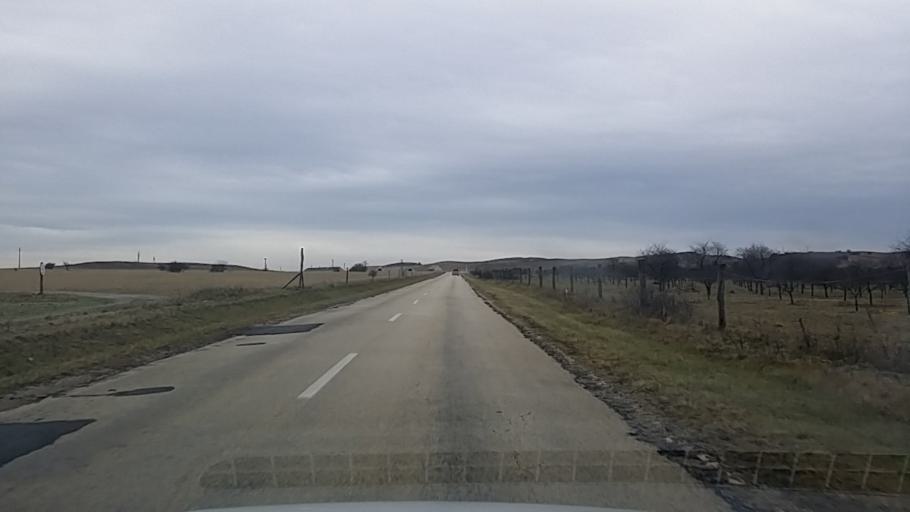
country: HU
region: Fejer
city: Zamoly
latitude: 47.3406
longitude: 18.3631
